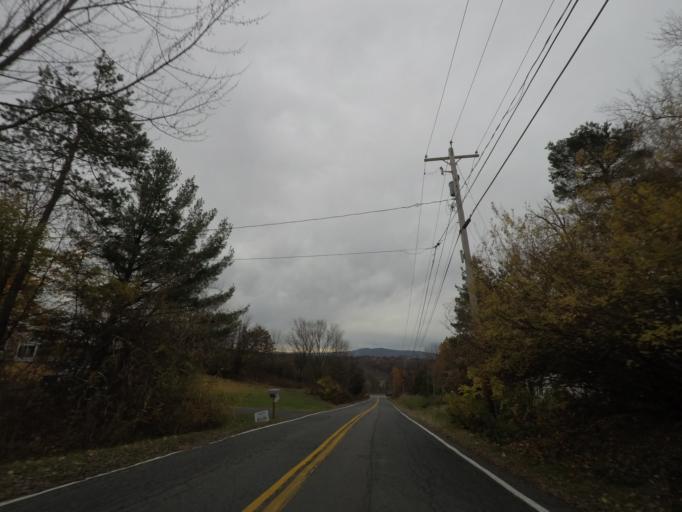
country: US
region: New York
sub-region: Albany County
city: Cohoes
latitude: 42.7945
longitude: -73.7181
